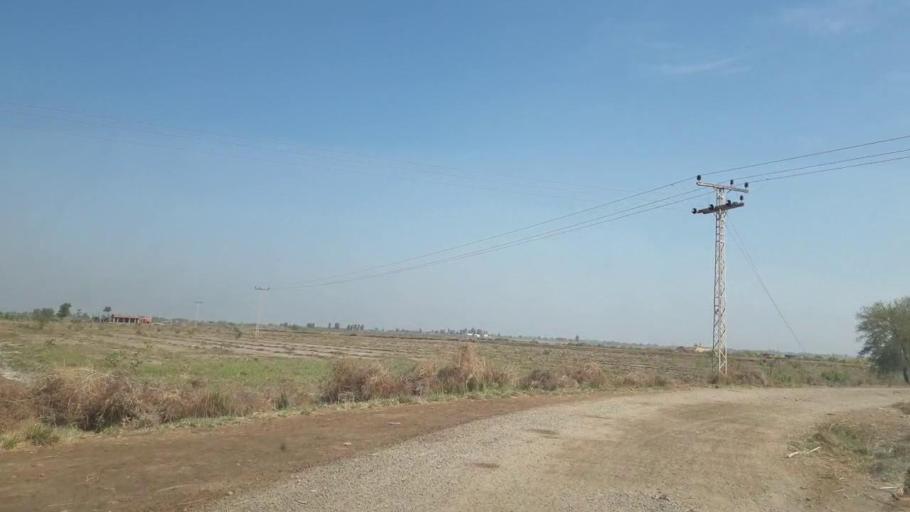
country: PK
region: Sindh
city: Mirpur Khas
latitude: 25.5655
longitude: 69.1836
